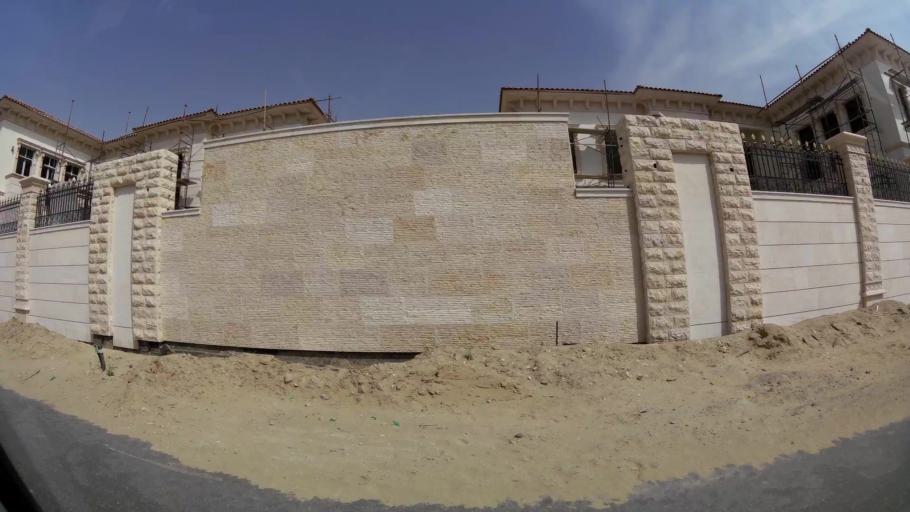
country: AE
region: Ash Shariqah
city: Sharjah
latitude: 25.2637
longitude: 55.4702
